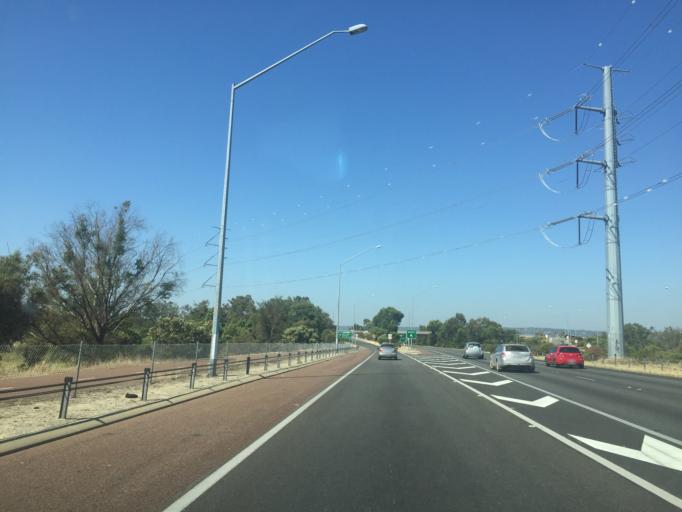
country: AU
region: Western Australia
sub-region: Gosnells
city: Kenwick
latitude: -32.0389
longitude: 115.9565
